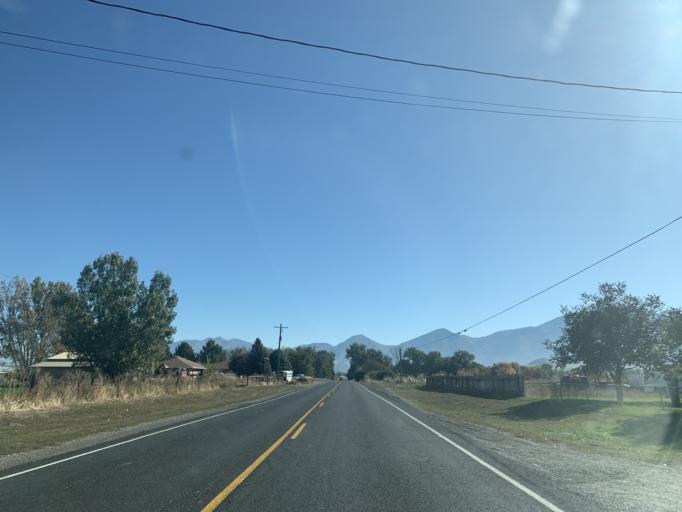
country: US
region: Utah
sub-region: Utah County
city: West Mountain
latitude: 40.0411
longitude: -111.7759
